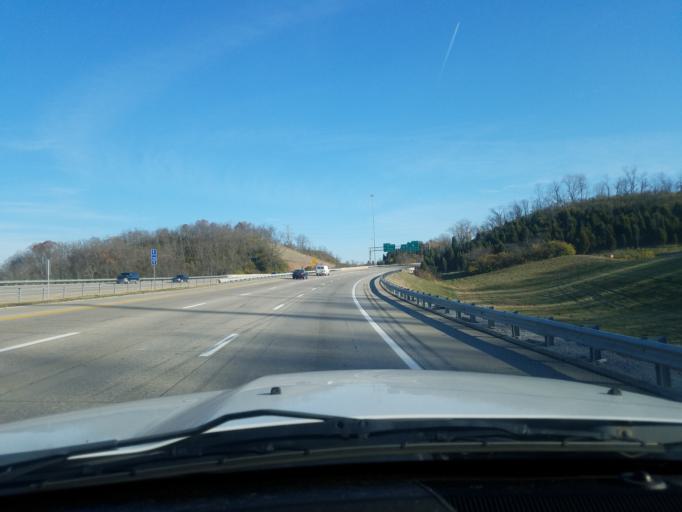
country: US
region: Kentucky
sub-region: Campbell County
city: Highland Heights
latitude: 39.0423
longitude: -84.4689
